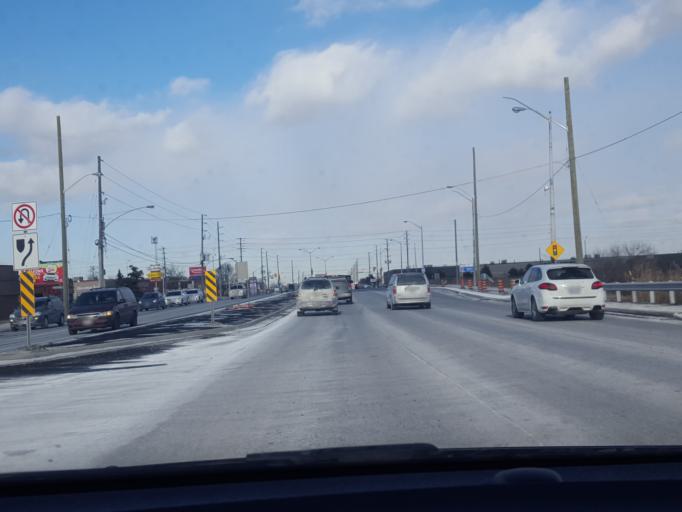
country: CA
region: Ontario
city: Brampton
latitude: 43.6883
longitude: -79.7088
